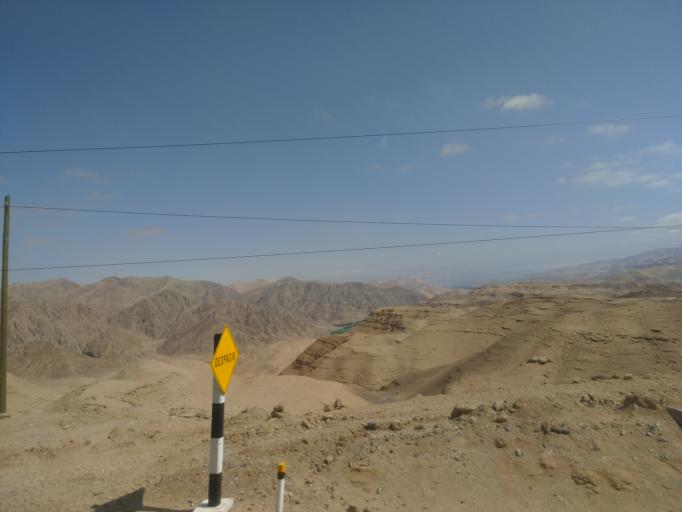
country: PE
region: Moquegua
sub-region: Provincia de Mariscal Nieto
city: Moquegua
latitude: -17.3898
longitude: -71.0120
